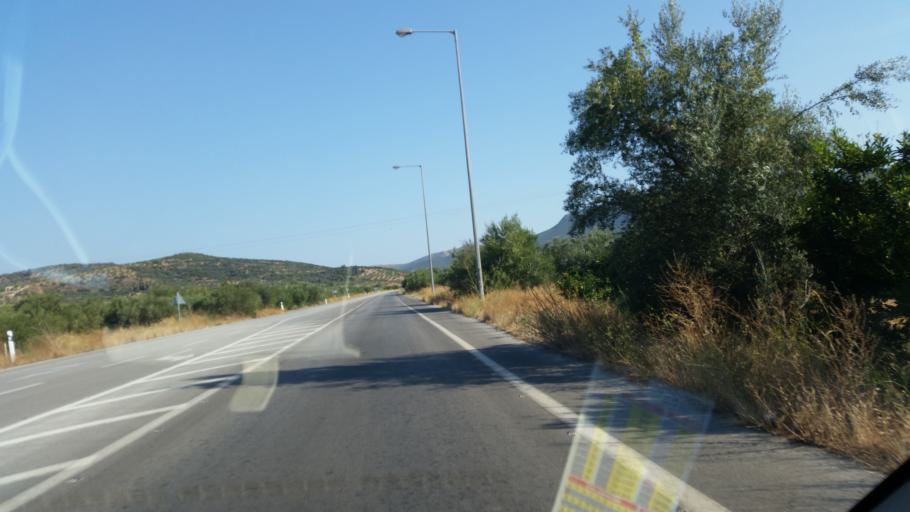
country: GR
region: Peloponnese
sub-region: Nomos Argolidos
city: Koutsopodi
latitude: 37.7197
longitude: 22.7353
